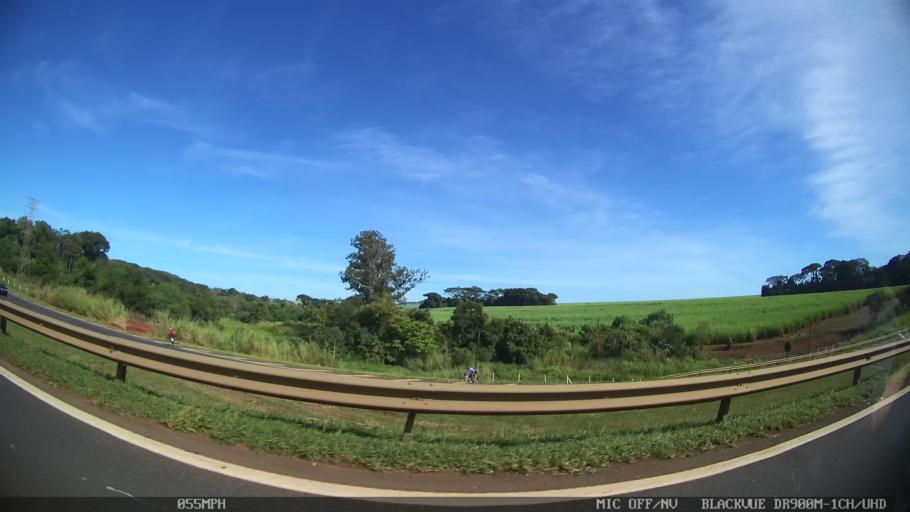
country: BR
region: Sao Paulo
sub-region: Araras
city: Araras
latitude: -22.3080
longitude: -47.3913
